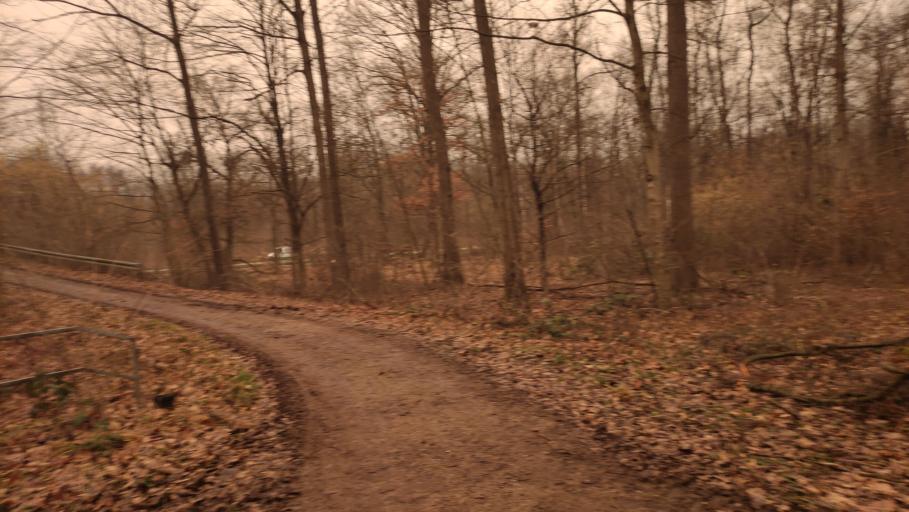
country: DE
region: Baden-Wuerttemberg
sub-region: Freiburg Region
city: Vorstetten
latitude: 48.0377
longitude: 7.8220
